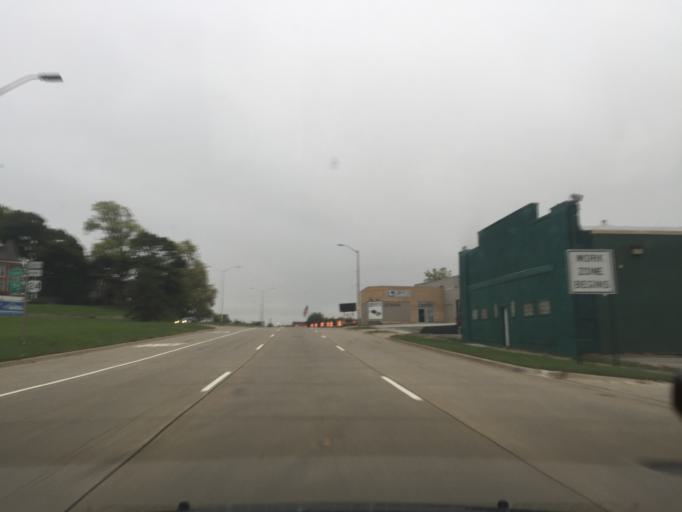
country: US
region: Michigan
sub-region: Oakland County
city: Pontiac
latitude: 42.6303
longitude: -83.2896
